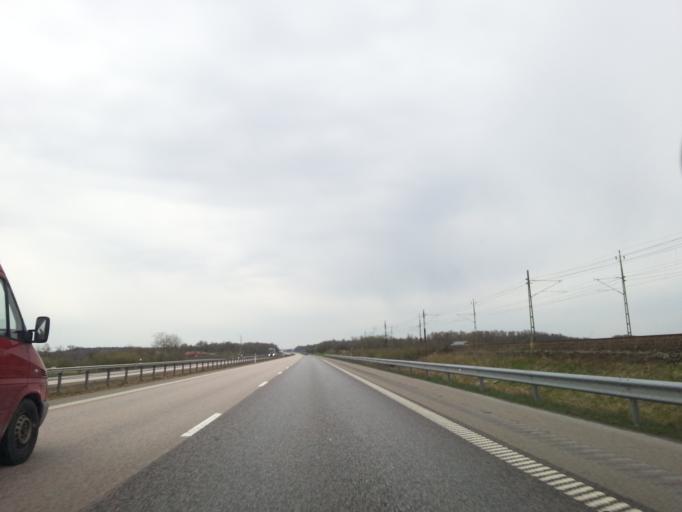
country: SE
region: Halland
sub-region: Varbergs Kommun
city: Tvaaker
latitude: 57.0120
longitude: 12.3979
